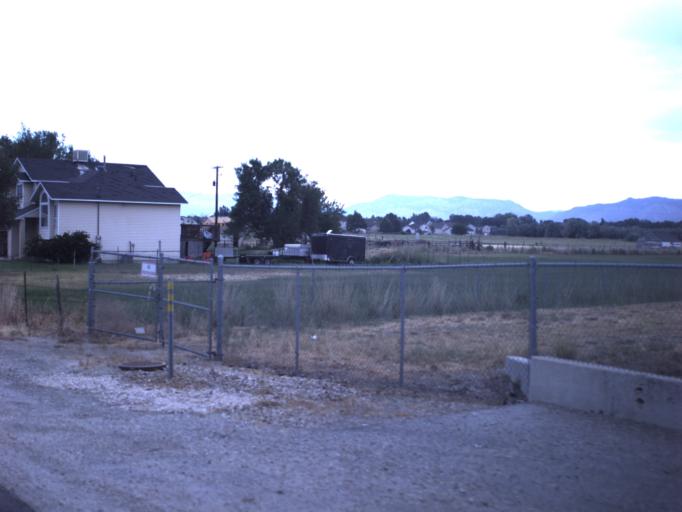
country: US
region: Utah
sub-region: Davis County
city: West Point
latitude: 41.1101
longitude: -112.1125
